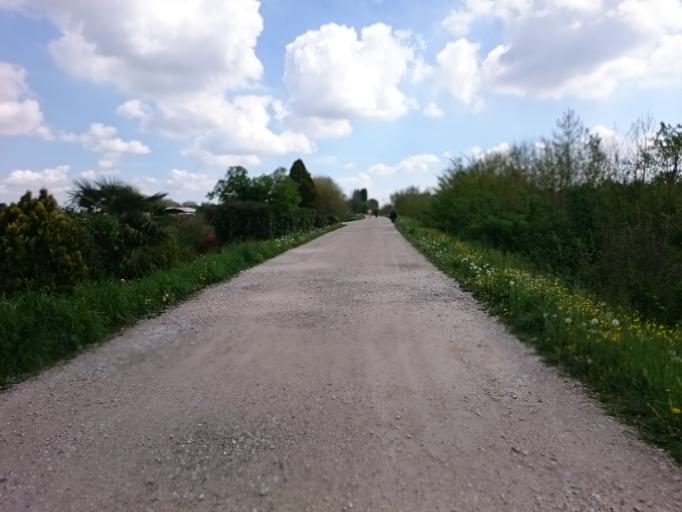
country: IT
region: Veneto
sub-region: Provincia di Padova
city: Selvazzano Dentro
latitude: 45.3977
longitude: 11.7920
